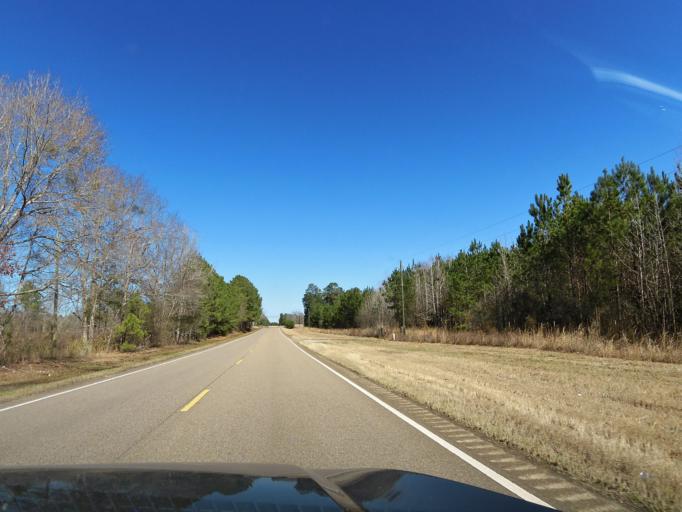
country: US
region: Alabama
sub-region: Bullock County
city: Union Springs
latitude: 32.1176
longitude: -85.7821
